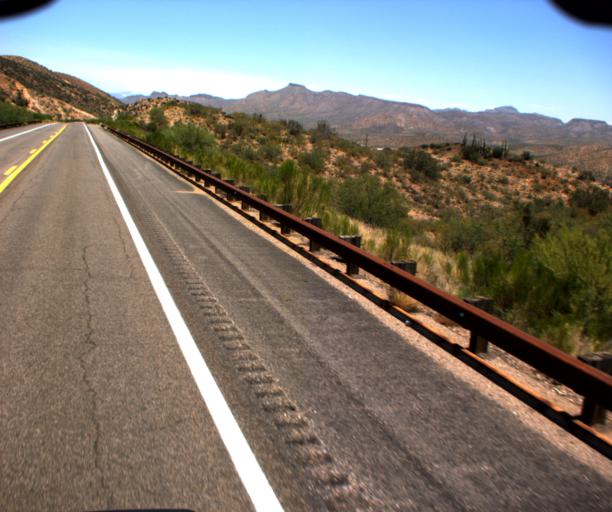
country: US
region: Arizona
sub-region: Gila County
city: Claypool
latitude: 33.4986
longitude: -110.8664
